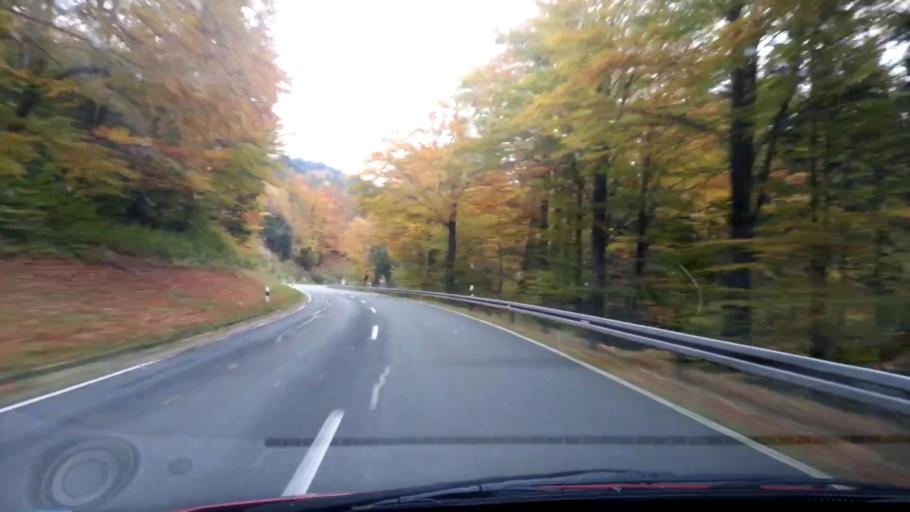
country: DE
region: Bavaria
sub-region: Upper Franconia
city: Warmensteinach
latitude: 49.9609
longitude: 11.7620
